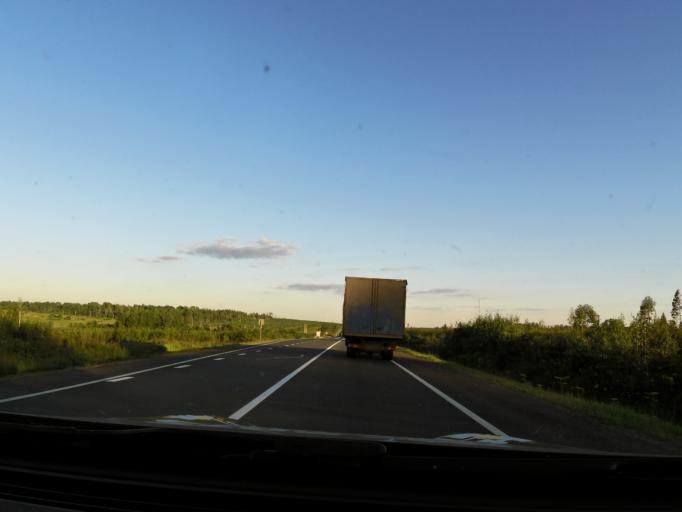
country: RU
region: Jaroslavl
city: Prechistoye
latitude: 58.6364
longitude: 40.3256
